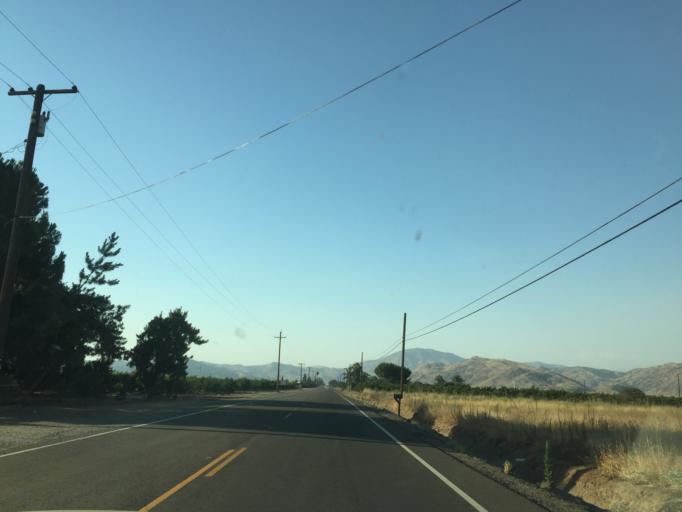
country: US
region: California
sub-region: Fresno County
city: Orange Cove
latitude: 36.6323
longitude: -119.3048
